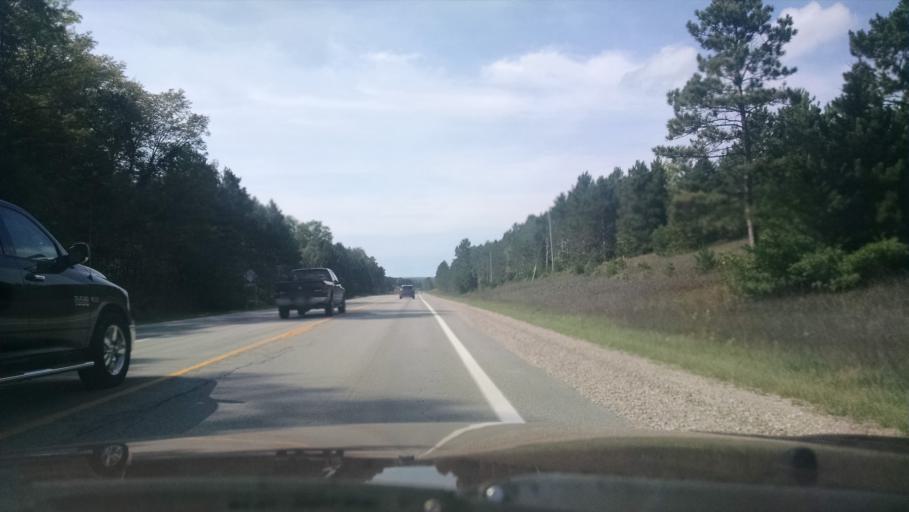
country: US
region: Michigan
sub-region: Grand Traverse County
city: Kingsley
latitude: 44.3879
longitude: -85.6716
